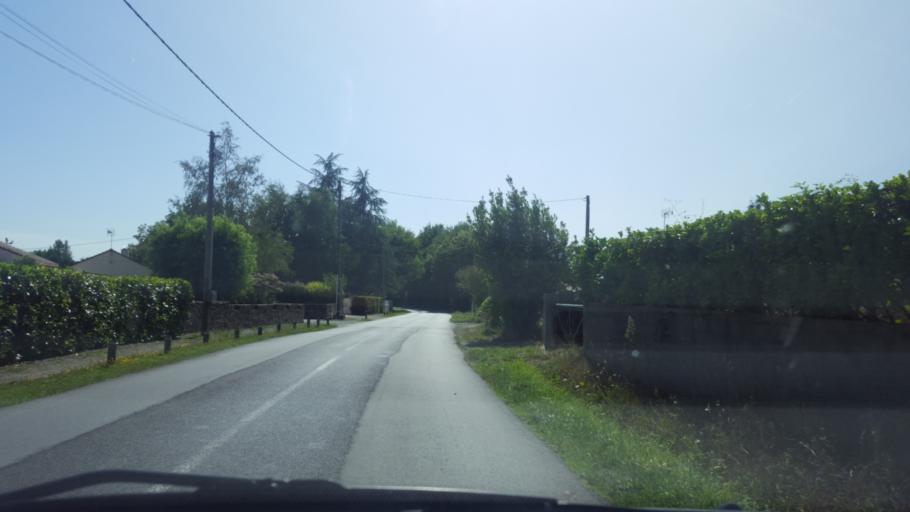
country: FR
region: Pays de la Loire
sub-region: Departement de la Loire-Atlantique
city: La Limouziniere
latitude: 47.0048
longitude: -1.5852
